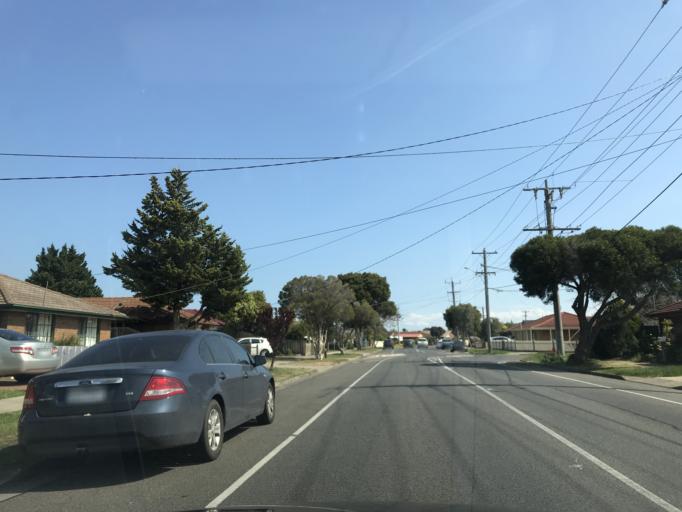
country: AU
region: Victoria
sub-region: Wyndham
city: Hoppers Crossing
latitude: -37.8735
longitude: 144.7091
